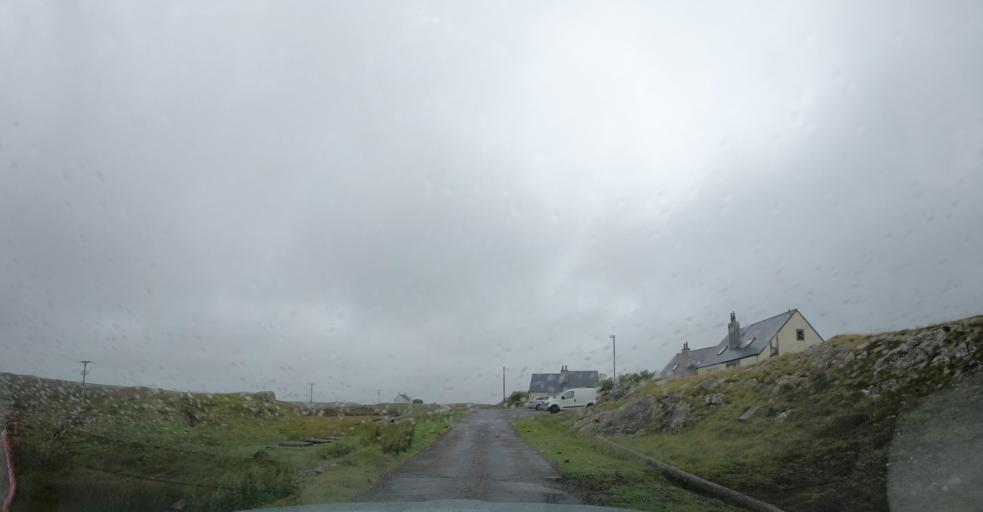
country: GB
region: Scotland
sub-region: Eilean Siar
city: Benbecula
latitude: 57.4898
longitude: -7.2228
